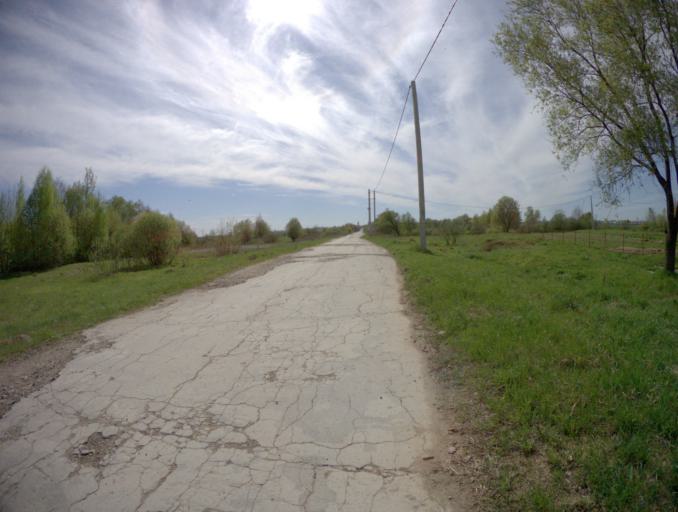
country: RU
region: Vladimir
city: Bogolyubovo
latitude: 56.2060
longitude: 40.5691
